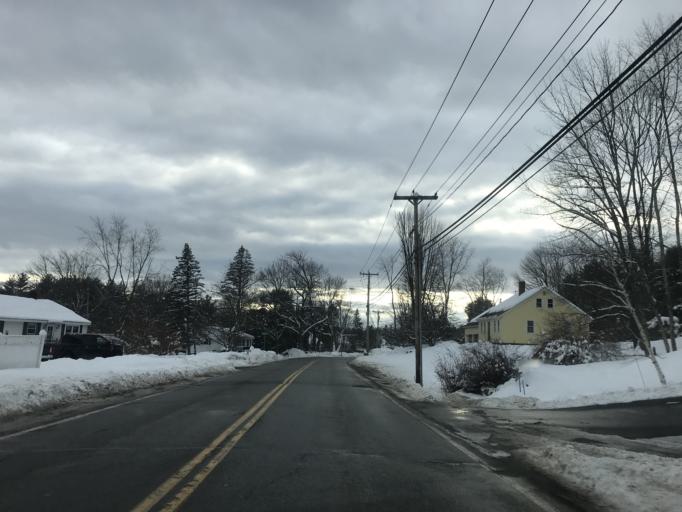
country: US
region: Maine
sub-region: Cumberland County
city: Westbrook
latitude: 43.7193
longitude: -70.3240
